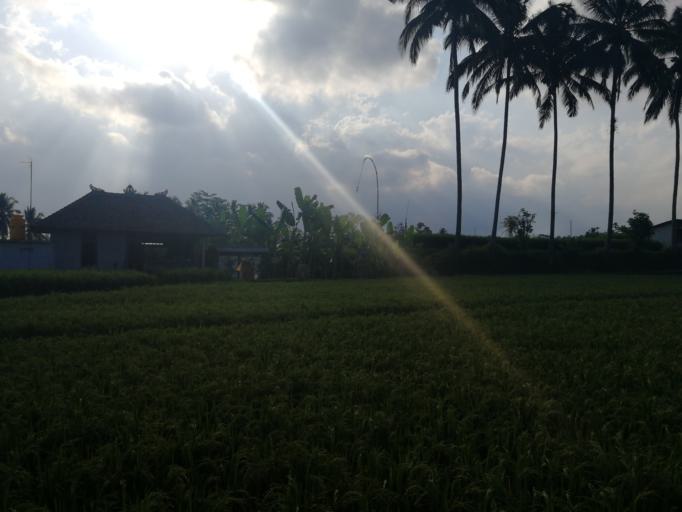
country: ID
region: Bali
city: Tegalalang
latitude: -8.4417
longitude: 115.2742
